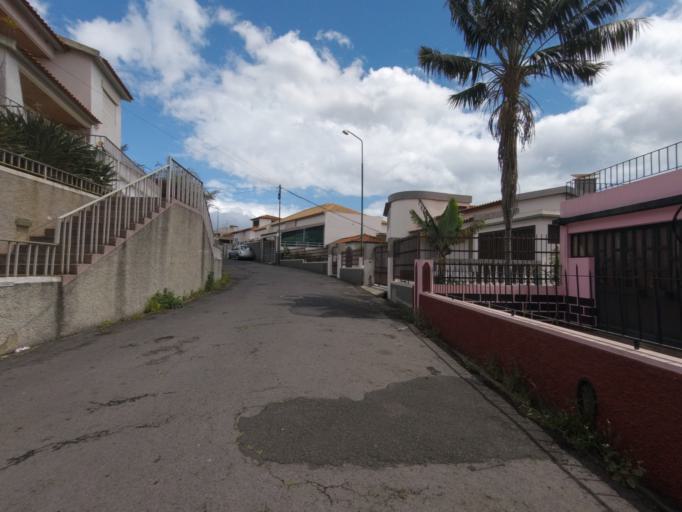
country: PT
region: Madeira
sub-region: Funchal
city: Nossa Senhora do Monte
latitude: 32.6675
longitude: -16.9114
